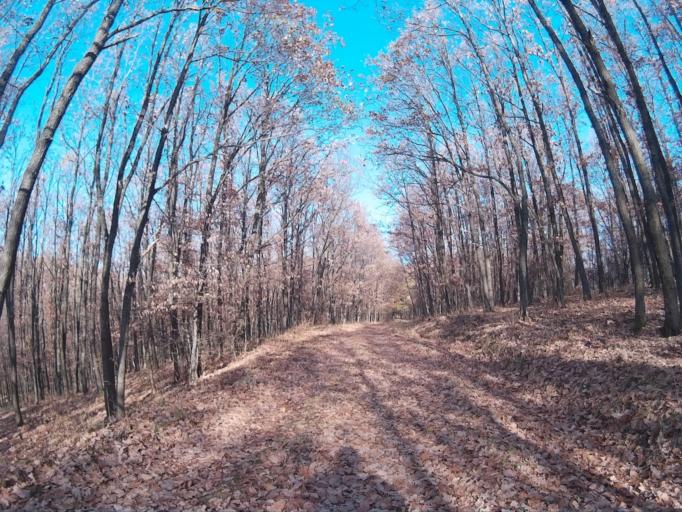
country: HU
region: Heves
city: Belapatfalva
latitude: 48.0224
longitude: 20.3958
